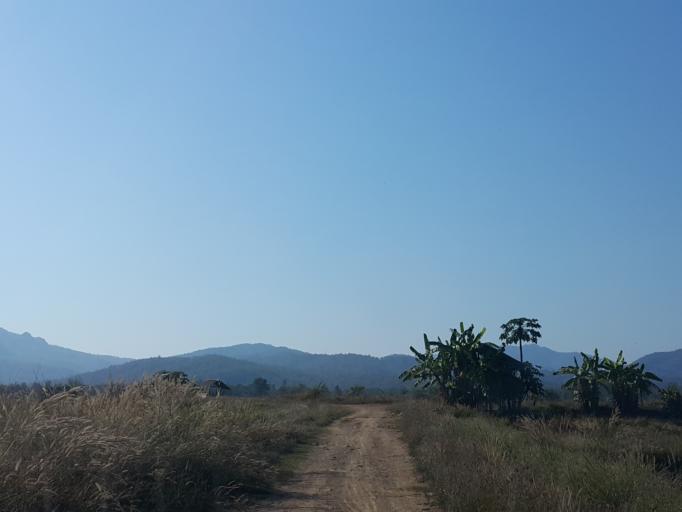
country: TH
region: Sukhothai
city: Thung Saliam
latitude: 17.3196
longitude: 99.4351
